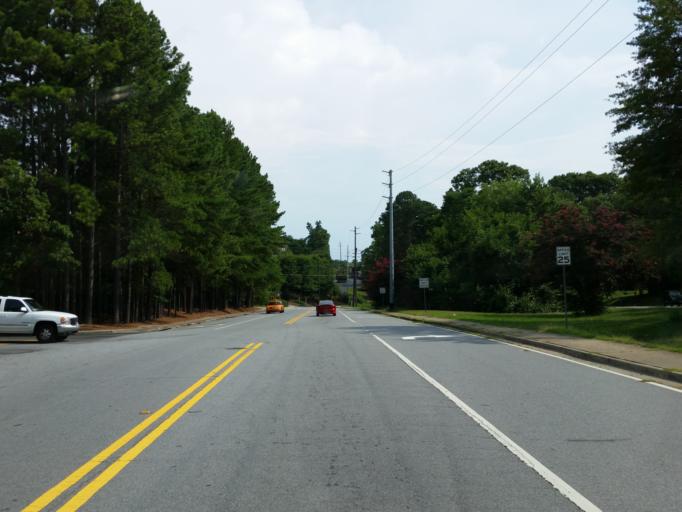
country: US
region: Georgia
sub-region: Cobb County
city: Marietta
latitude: 33.9466
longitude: -84.5238
